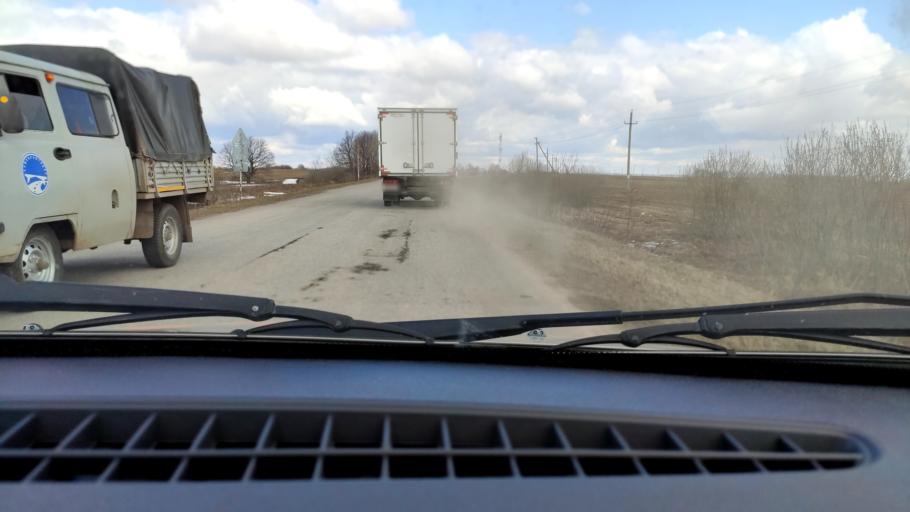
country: RU
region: Bashkortostan
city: Kudeyevskiy
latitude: 54.8336
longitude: 56.7929
